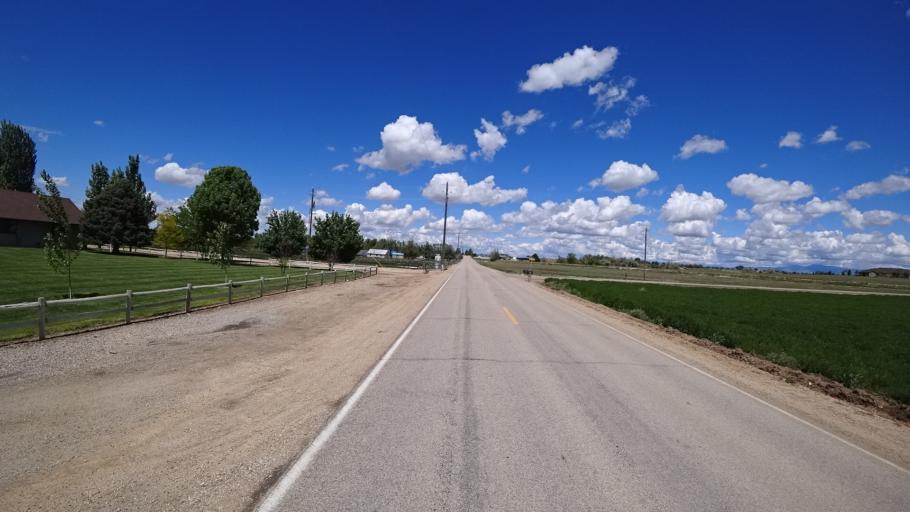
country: US
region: Idaho
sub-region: Ada County
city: Kuna
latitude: 43.5535
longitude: -116.4537
